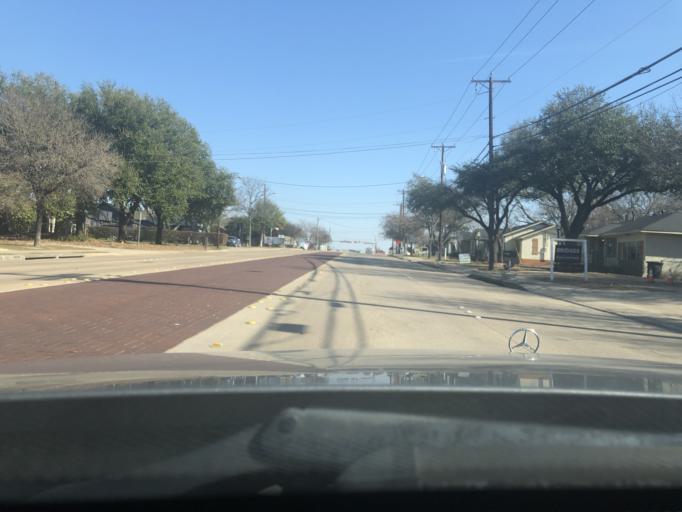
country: US
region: Texas
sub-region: Dallas County
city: Cedar Hill
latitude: 32.5900
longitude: -96.9496
